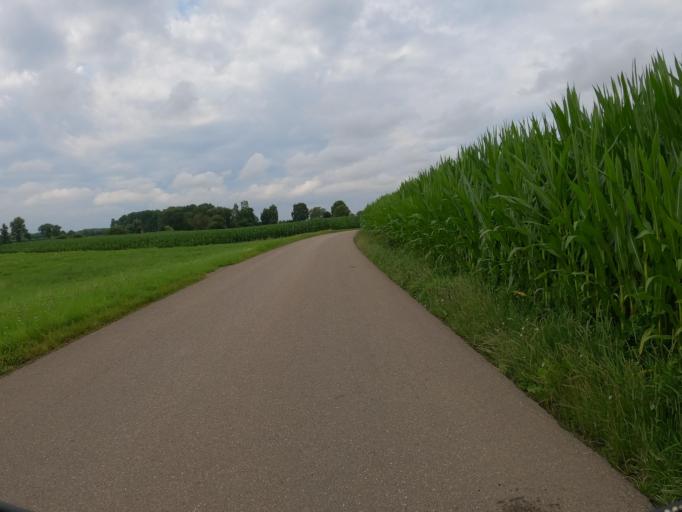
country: DE
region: Baden-Wuerttemberg
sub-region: Tuebingen Region
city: Rammingen
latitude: 48.5028
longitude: 10.1646
